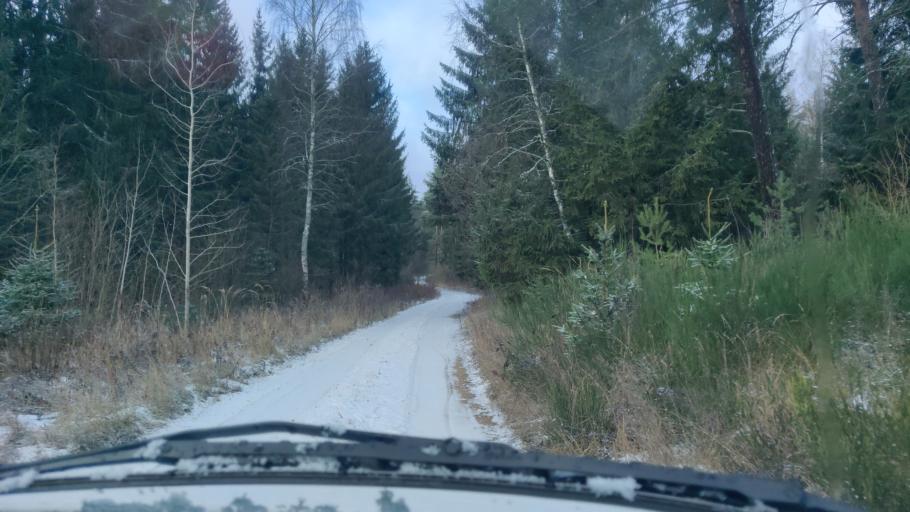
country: LT
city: Trakai
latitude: 54.5816
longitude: 24.9628
